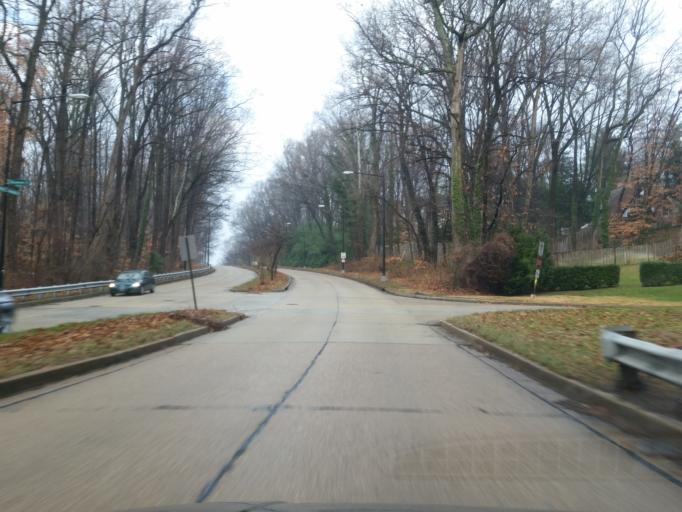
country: US
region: Maryland
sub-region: Montgomery County
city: Brookmont
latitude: 38.9386
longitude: -77.1041
